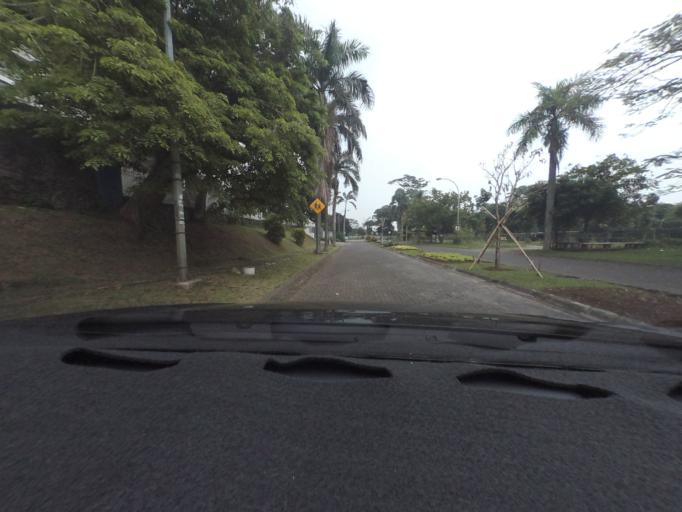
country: ID
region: West Java
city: Bogor
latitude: -6.5979
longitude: 106.8212
